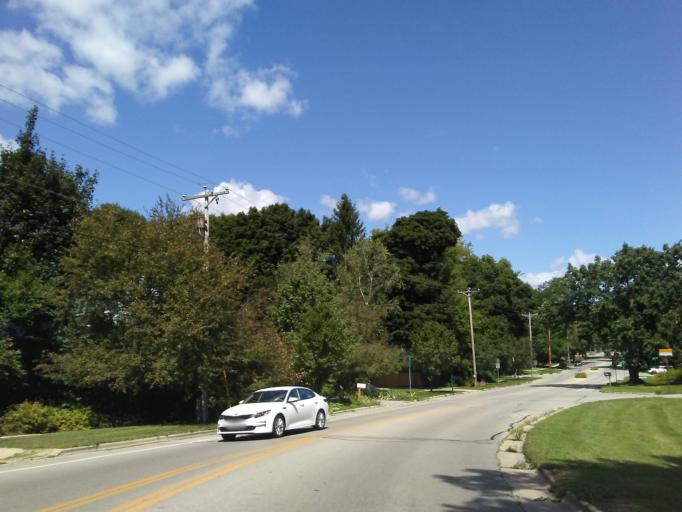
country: US
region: Wisconsin
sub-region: Dane County
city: Shorewood Hills
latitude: 43.0390
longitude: -89.4435
